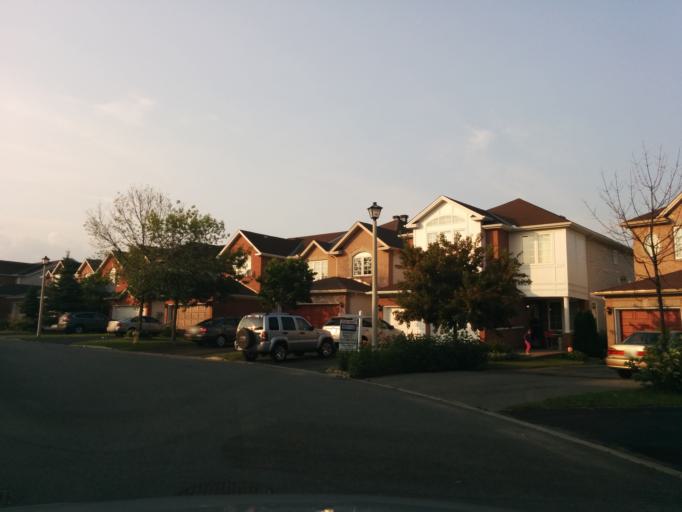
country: CA
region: Ontario
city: Ottawa
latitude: 45.3682
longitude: -75.7386
